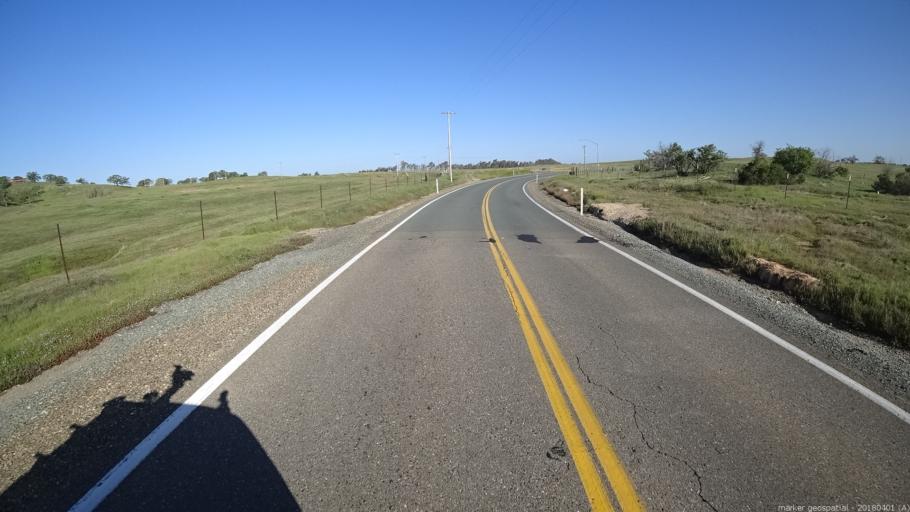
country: US
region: California
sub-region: Sacramento County
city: Rancho Murieta
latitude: 38.4261
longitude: -121.0539
